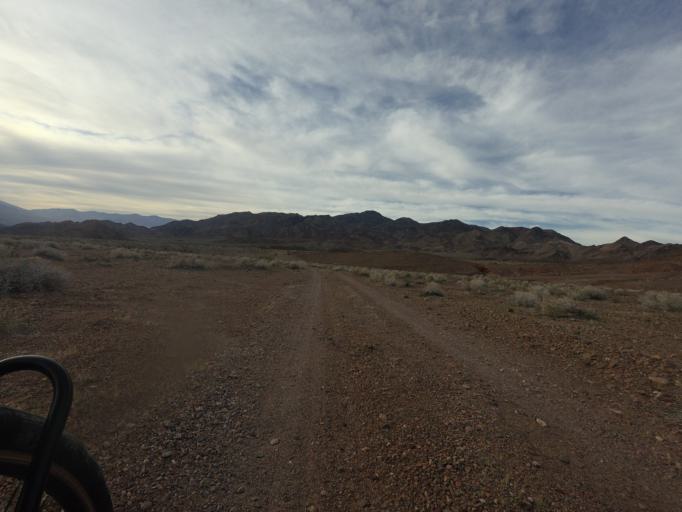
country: US
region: California
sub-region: San Bernardino County
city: Fort Irwin
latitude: 35.9126
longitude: -116.5863
